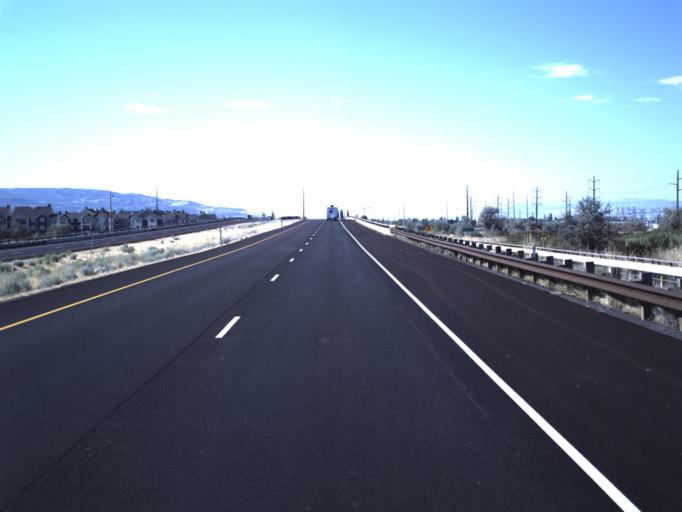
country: US
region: Utah
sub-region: Davis County
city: Centerville
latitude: 40.9246
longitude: -111.8995
